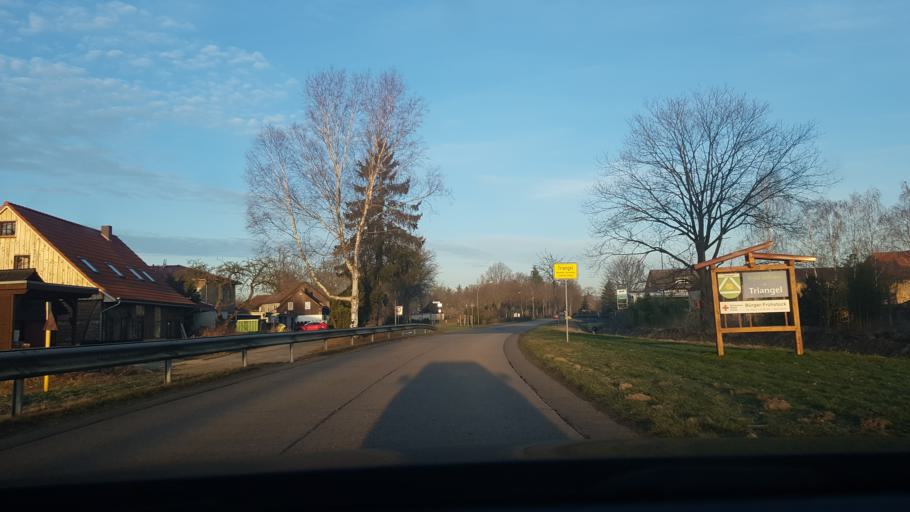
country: DE
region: Lower Saxony
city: Sassenburg
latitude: 52.5069
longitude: 10.5919
